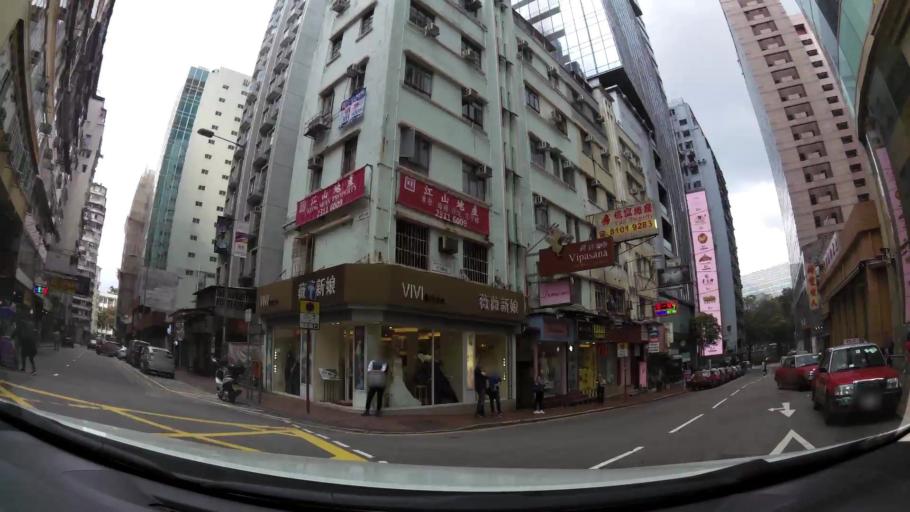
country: HK
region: Kowloon City
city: Kowloon
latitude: 22.3011
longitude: 114.1745
